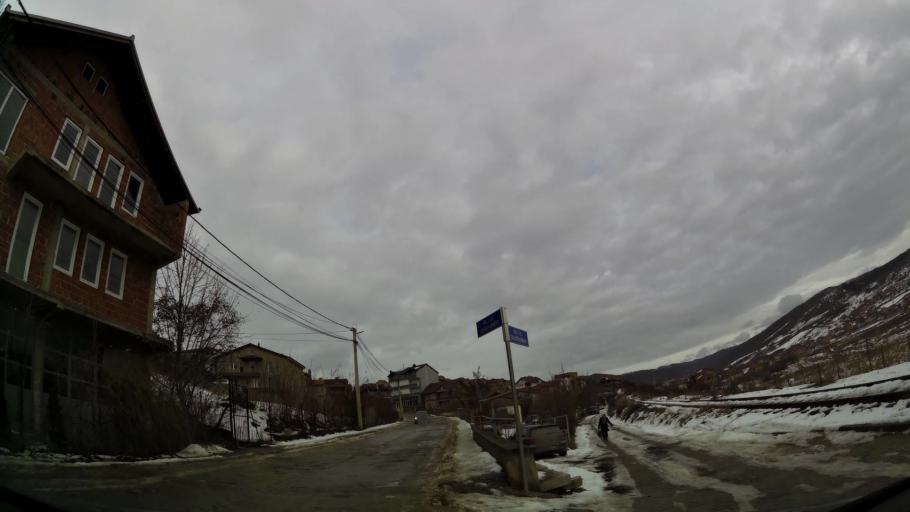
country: XK
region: Pristina
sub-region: Komuna e Prishtines
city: Pristina
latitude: 42.6838
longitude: 21.1740
